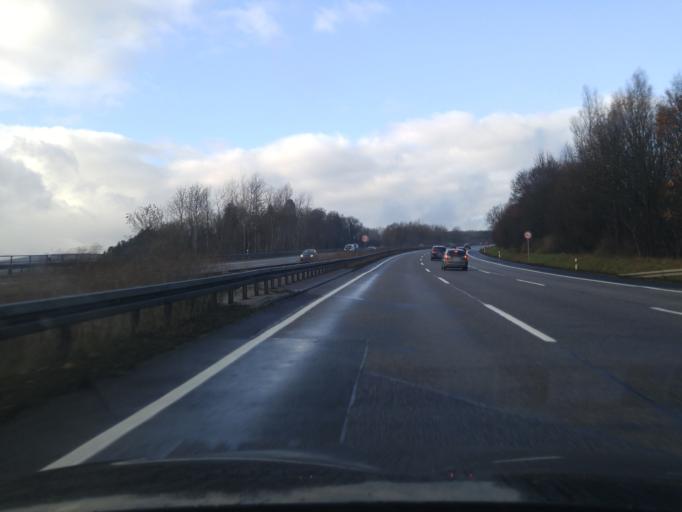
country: DE
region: Hesse
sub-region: Regierungsbezirk Kassel
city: Kirchheim
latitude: 50.9174
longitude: 9.5625
